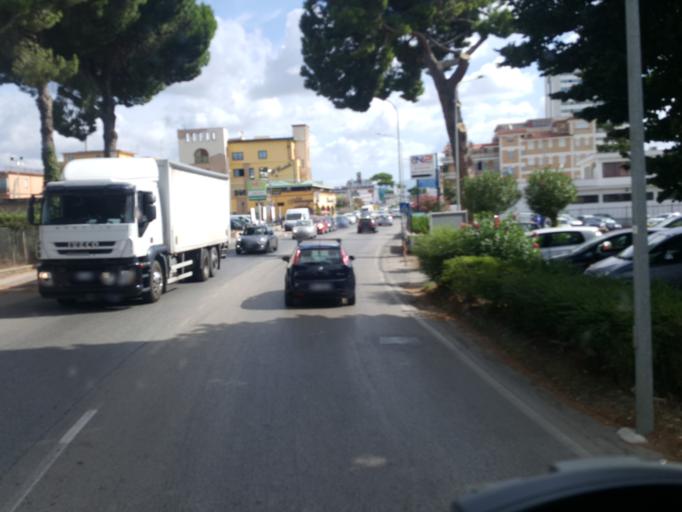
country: IT
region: Latium
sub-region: Citta metropolitana di Roma Capitale
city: Area Produttiva
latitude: 41.6803
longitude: 12.5028
